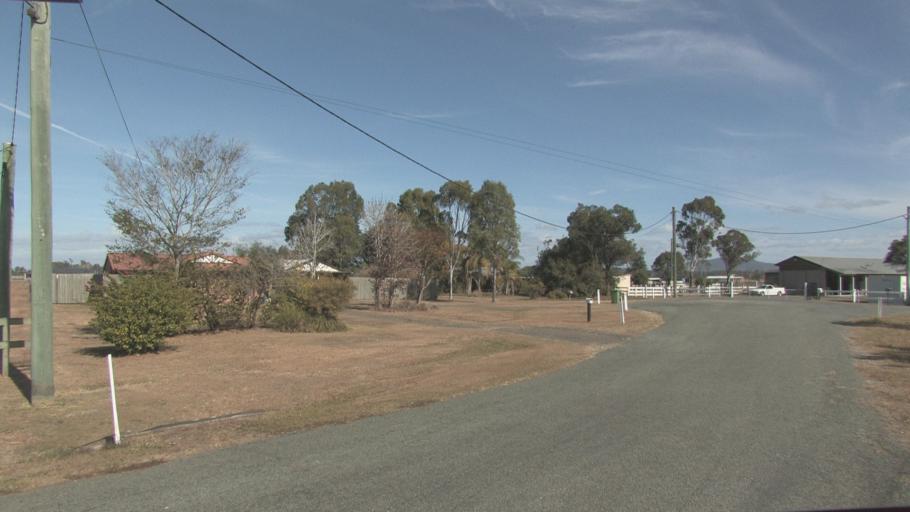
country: AU
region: Queensland
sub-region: Logan
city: Cedar Vale
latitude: -27.8695
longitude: 152.9640
